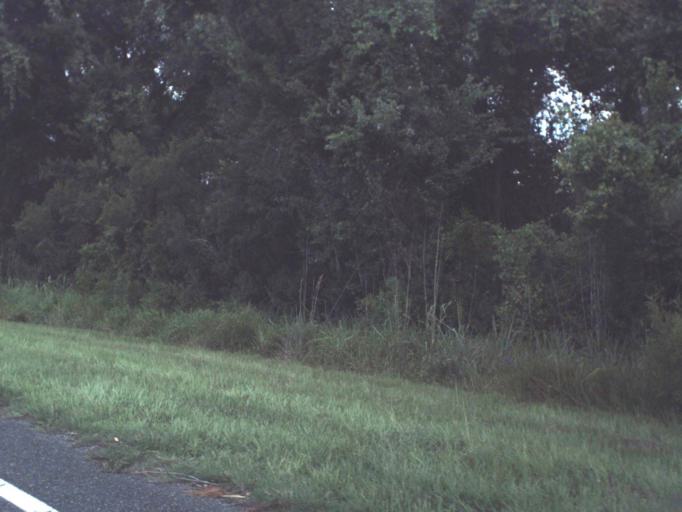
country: US
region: Florida
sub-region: Taylor County
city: Steinhatchee
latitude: 29.8485
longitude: -83.3778
